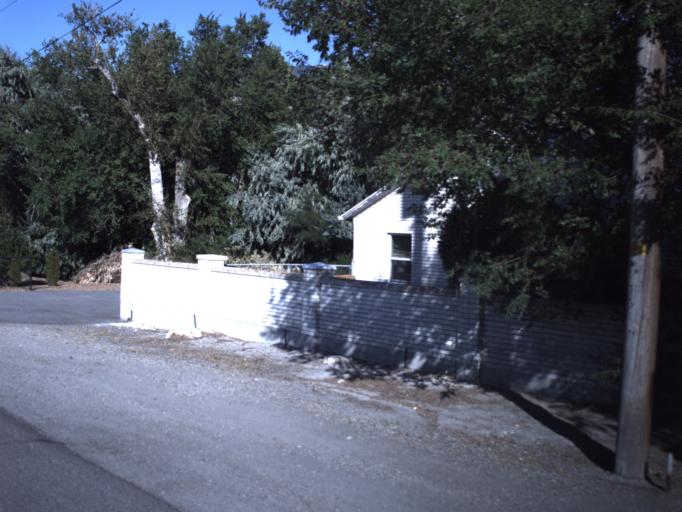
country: US
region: Utah
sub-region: Tooele County
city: Stansbury park
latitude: 40.6493
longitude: -112.2987
